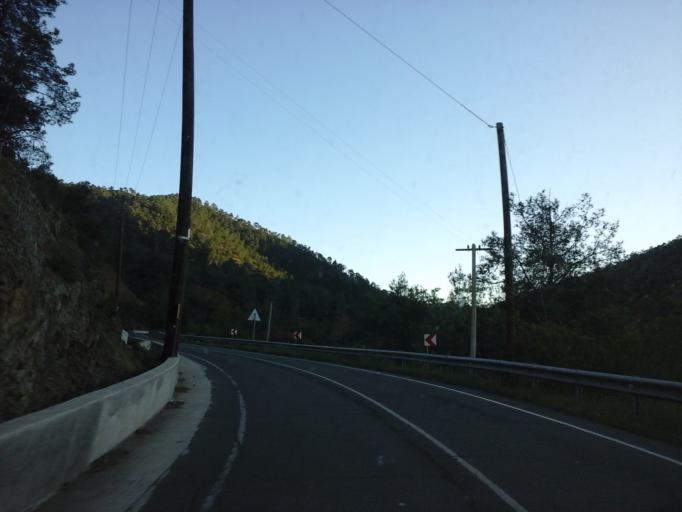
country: CY
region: Lefkosia
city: Astromeritis
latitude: 35.0628
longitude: 32.9885
